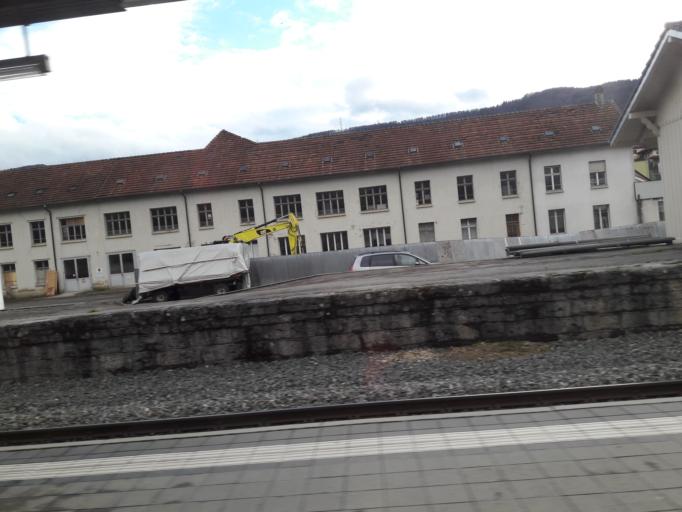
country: CH
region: Jura
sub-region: Delemont District
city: Courfaivre
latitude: 47.3352
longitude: 7.2916
